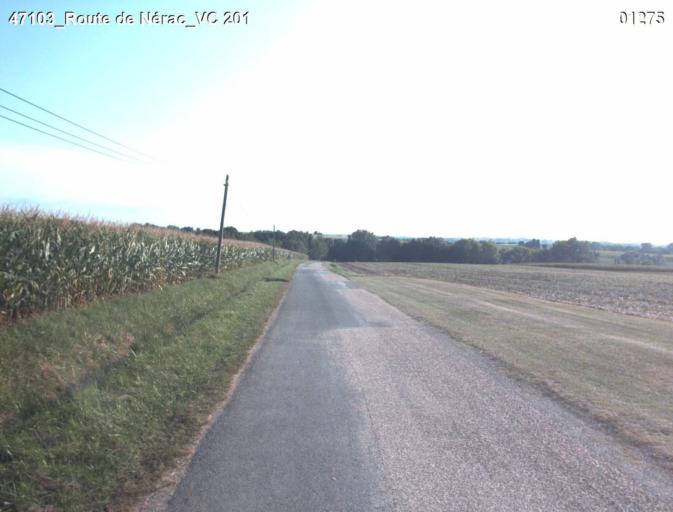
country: FR
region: Aquitaine
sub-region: Departement du Lot-et-Garonne
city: Nerac
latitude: 44.0888
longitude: 0.3336
